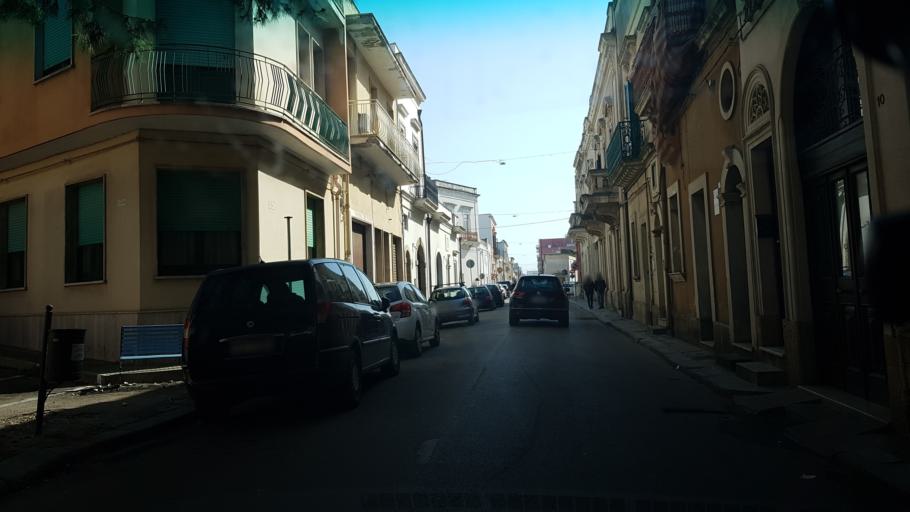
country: IT
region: Apulia
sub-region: Provincia di Brindisi
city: San Pietro Vernotico
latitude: 40.4870
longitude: 17.9983
